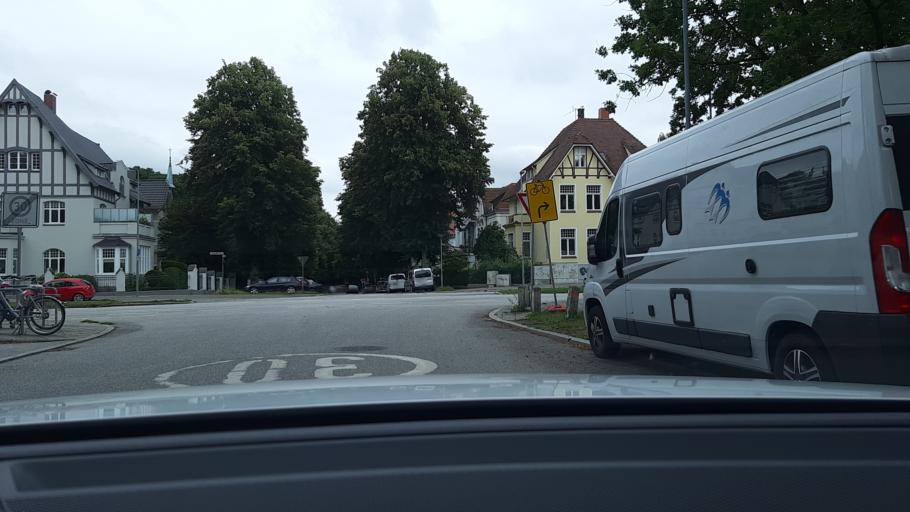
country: DE
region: Schleswig-Holstein
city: Luebeck
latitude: 53.8814
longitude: 10.6988
